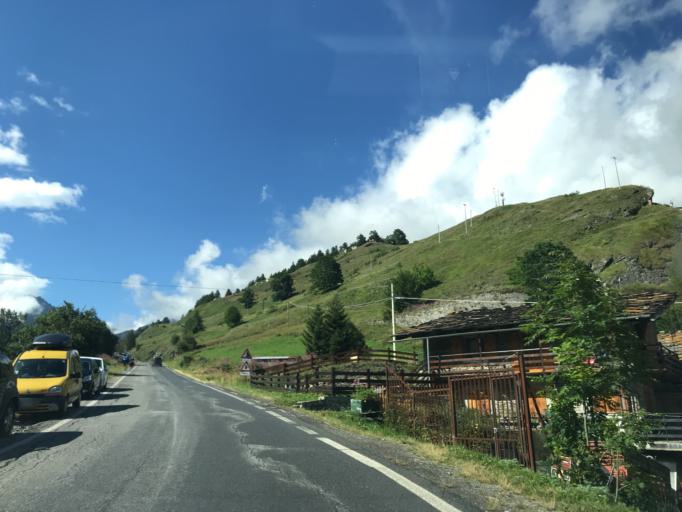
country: IT
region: Piedmont
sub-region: Provincia di Cuneo
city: Pontechianale
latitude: 44.6255
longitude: 7.0235
